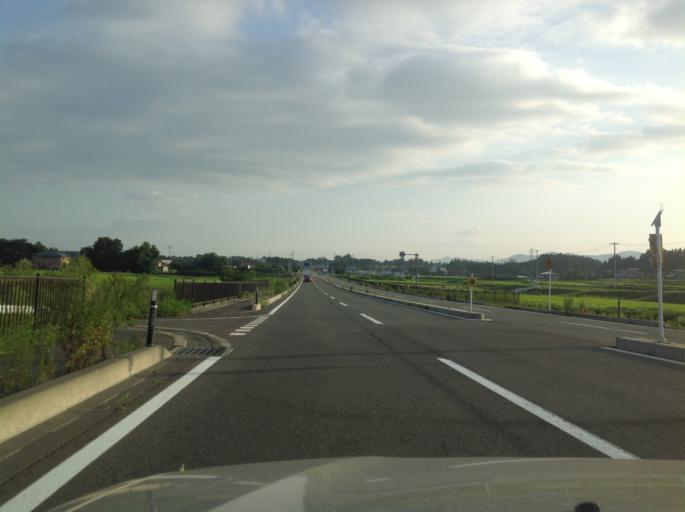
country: JP
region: Iwate
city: Hanamaki
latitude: 39.5071
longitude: 141.1499
